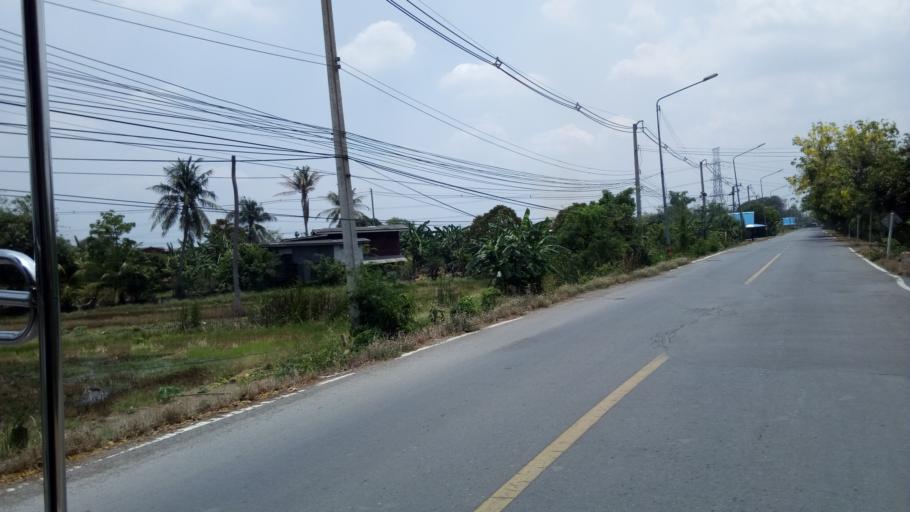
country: TH
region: Pathum Thani
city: Sam Khok
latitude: 14.1091
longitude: 100.5388
